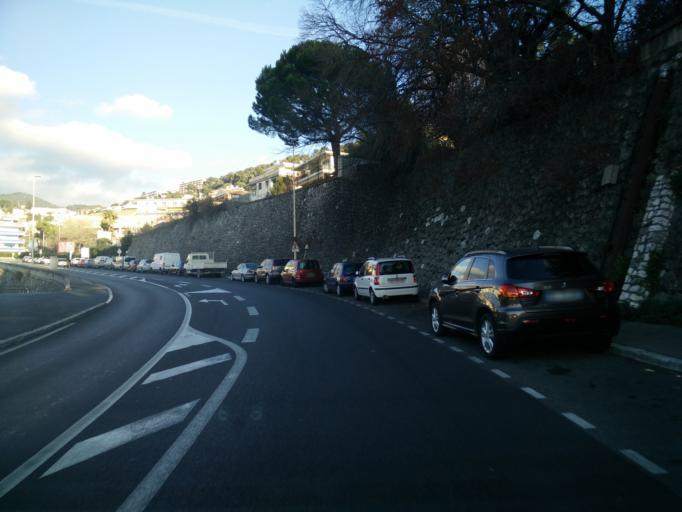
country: FR
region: Provence-Alpes-Cote d'Azur
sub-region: Departement des Alpes-Maritimes
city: Villefranche-sur-Mer
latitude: 43.7012
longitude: 7.2919
